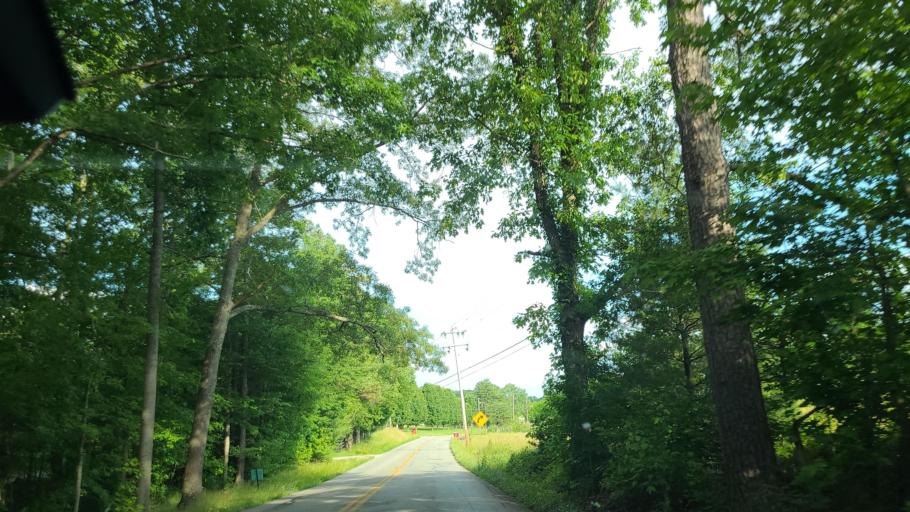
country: US
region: Kentucky
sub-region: Whitley County
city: Corbin
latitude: 36.9049
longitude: -84.2390
